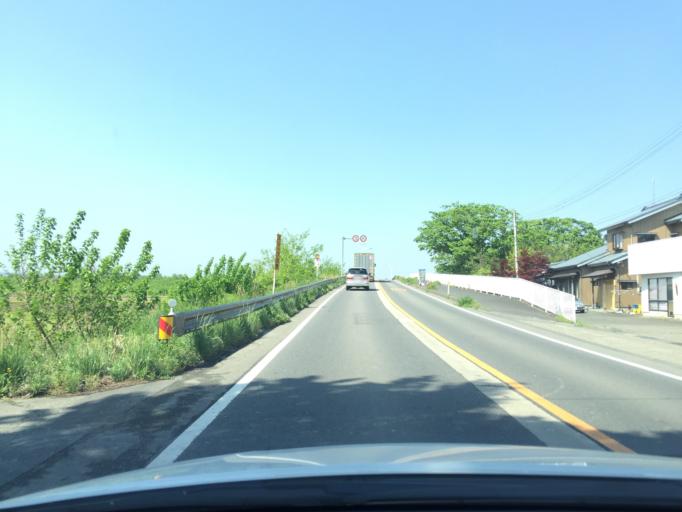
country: JP
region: Niigata
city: Muramatsu
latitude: 37.7132
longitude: 139.2118
